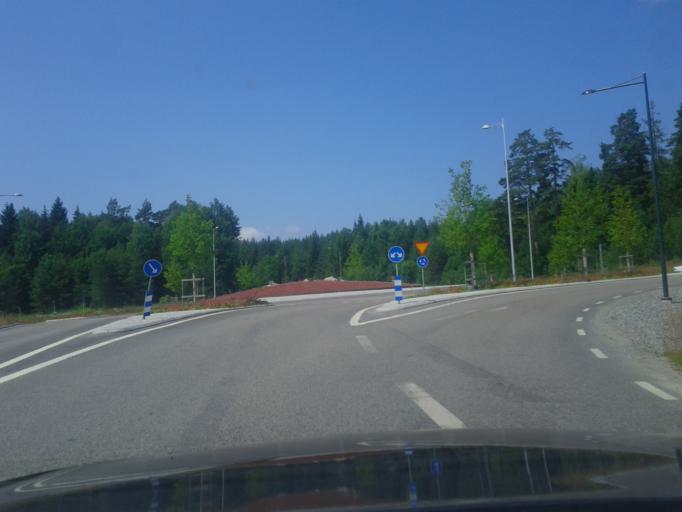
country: SE
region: Stockholm
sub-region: Taby Kommun
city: Taby
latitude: 59.4723
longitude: 18.1186
